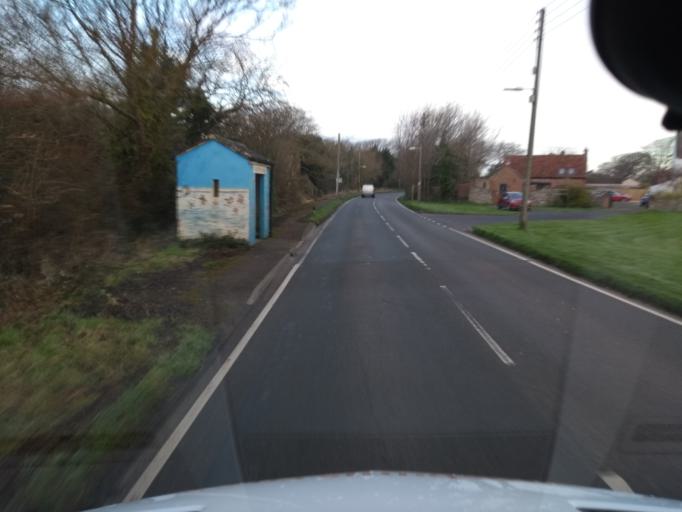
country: GB
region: England
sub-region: Somerset
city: Burnham-on-Sea
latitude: 51.2744
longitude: -3.0122
